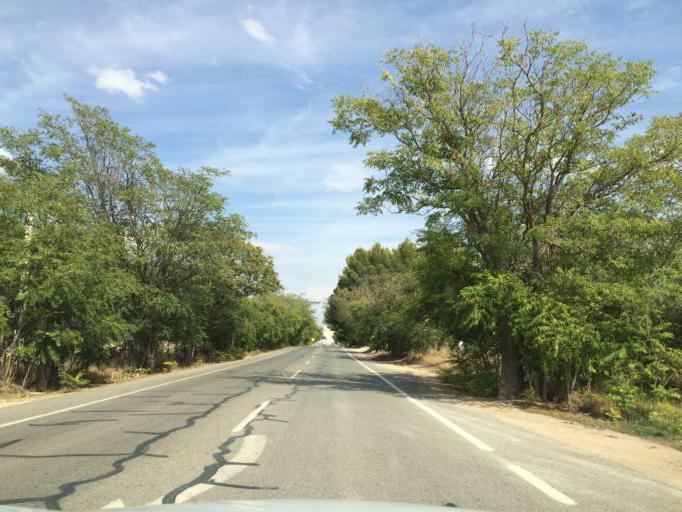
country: ES
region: Castille-La Mancha
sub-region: Provincia de Albacete
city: Albacete
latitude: 38.9974
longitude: -1.8849
